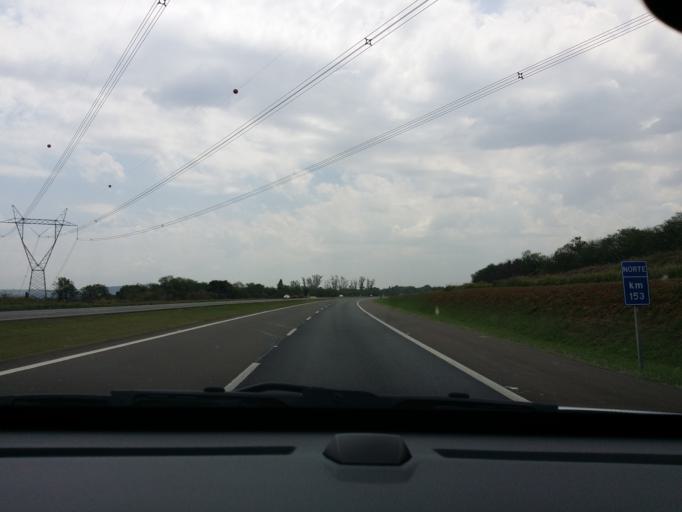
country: BR
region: Sao Paulo
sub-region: Iracemapolis
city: Iracemapolis
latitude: -22.6117
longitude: -47.4606
